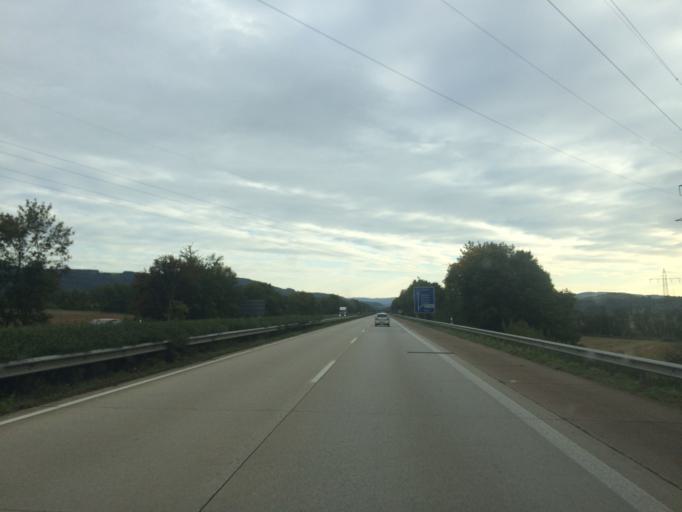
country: DE
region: Rheinland-Pfalz
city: Esch
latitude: 49.9118
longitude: 6.8546
